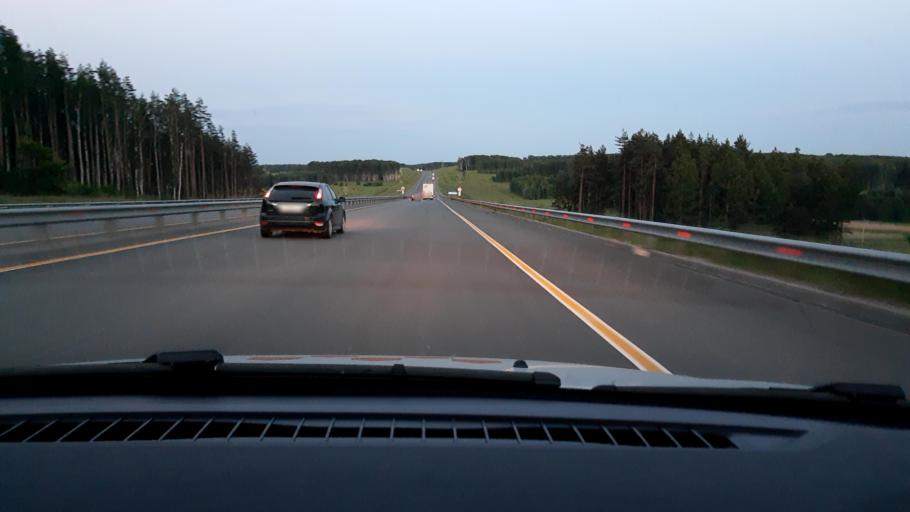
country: RU
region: Nizjnij Novgorod
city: Kstovo
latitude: 56.0814
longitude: 44.0966
